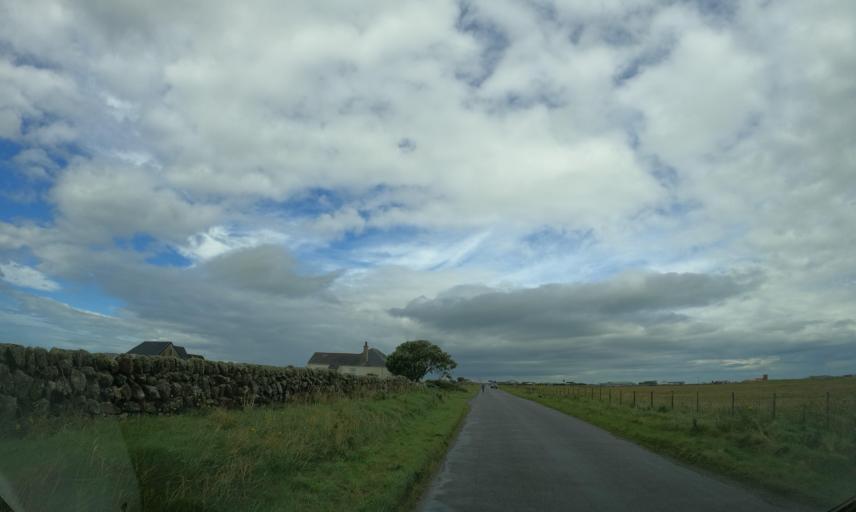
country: GB
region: Scotland
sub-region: Eilean Siar
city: Barra
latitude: 56.4923
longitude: -6.8827
